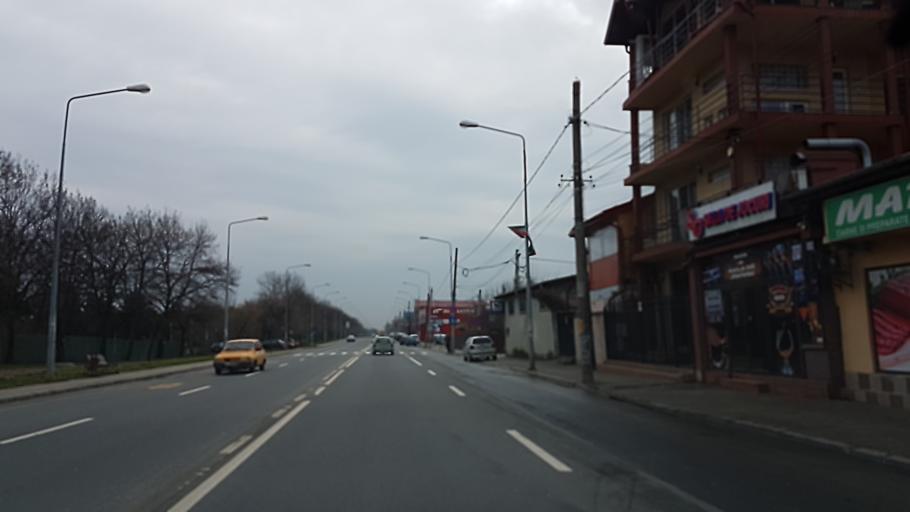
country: RO
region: Ilfov
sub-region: Comuna Pantelimon
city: Pantelimon
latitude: 44.4381
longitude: 26.1970
